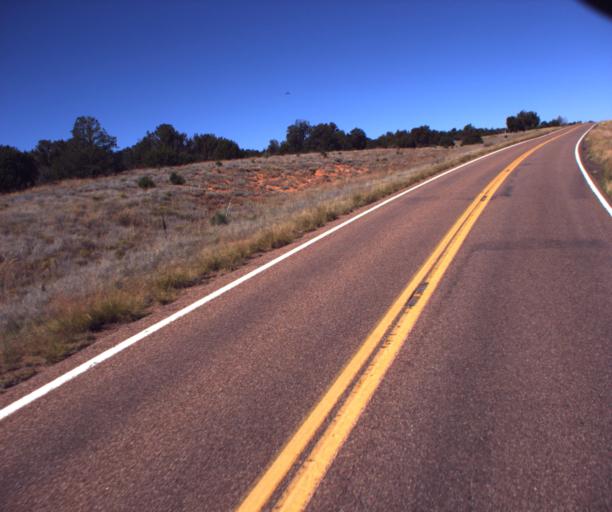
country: US
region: Arizona
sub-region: Navajo County
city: Heber-Overgaard
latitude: 34.4541
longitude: -110.4621
